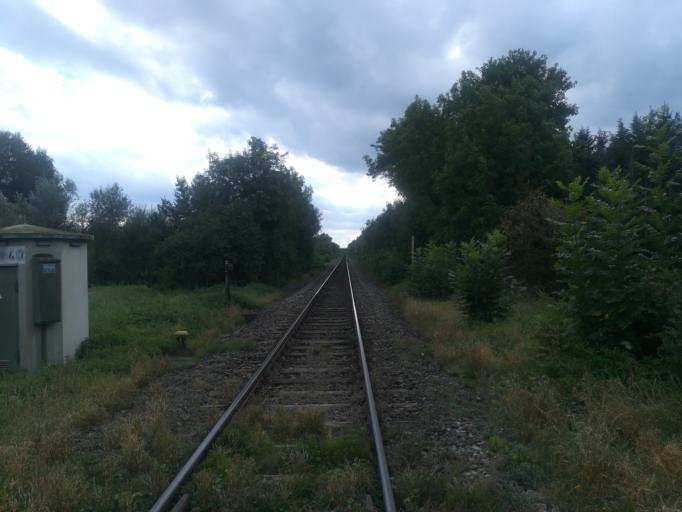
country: DE
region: Baden-Wuerttemberg
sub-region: Tuebingen Region
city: Riedlingen
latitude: 48.1601
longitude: 9.4940
